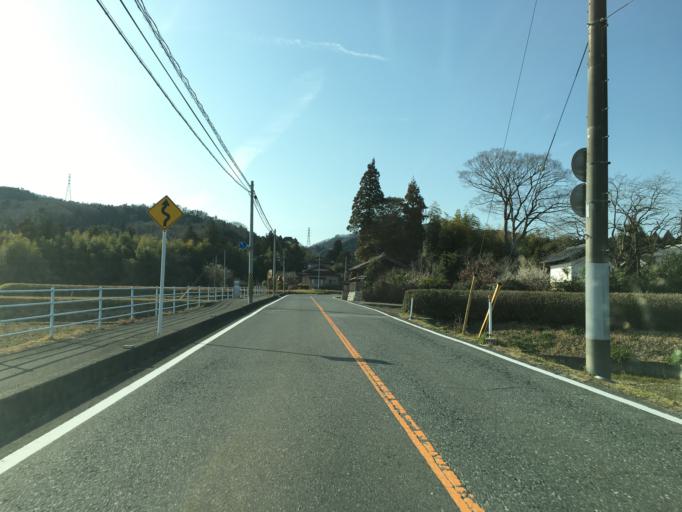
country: JP
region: Ibaraki
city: Takahagi
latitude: 36.7221
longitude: 140.6766
